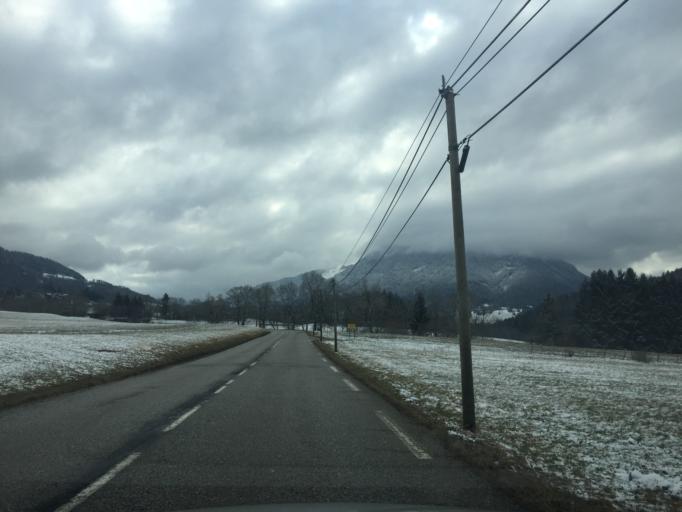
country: FR
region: Rhone-Alpes
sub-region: Departement de la Haute-Savoie
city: Gruffy
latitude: 45.7088
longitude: 6.1158
